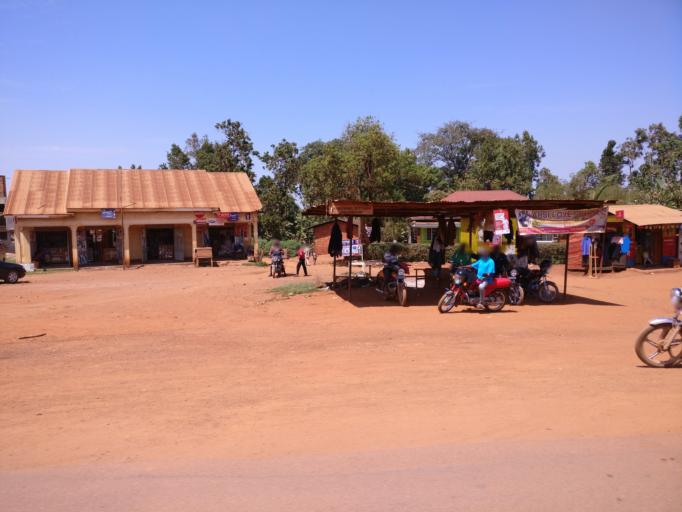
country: UG
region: Central Region
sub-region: Wakiso District
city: Entebbe
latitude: 0.1069
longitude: 32.5220
